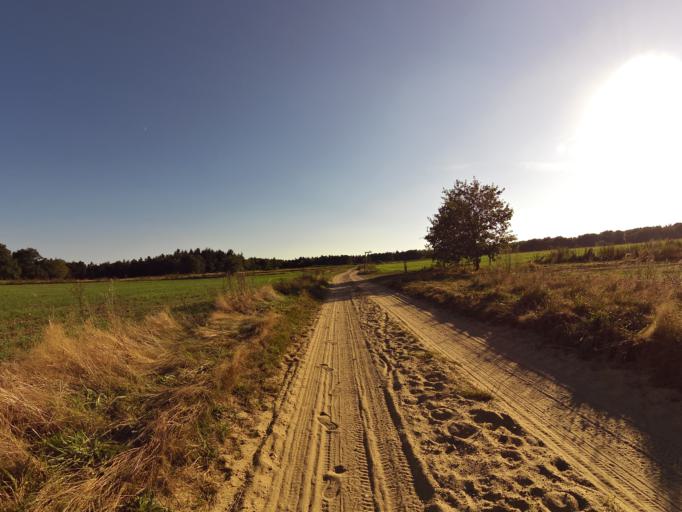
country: NL
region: Gelderland
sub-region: Gemeente Montferland
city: s-Heerenberg
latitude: 51.9040
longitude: 6.2448
